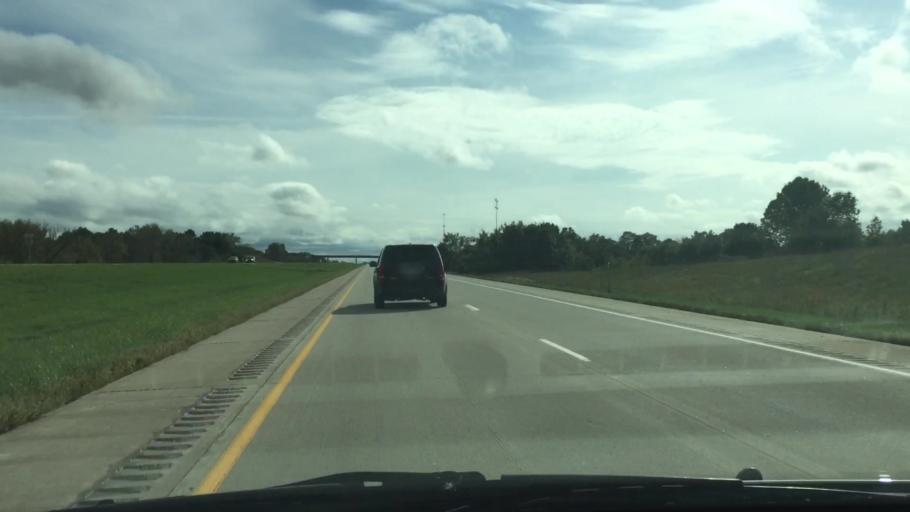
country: US
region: Iowa
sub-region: Decatur County
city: Leon
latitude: 40.8785
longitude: -93.8019
